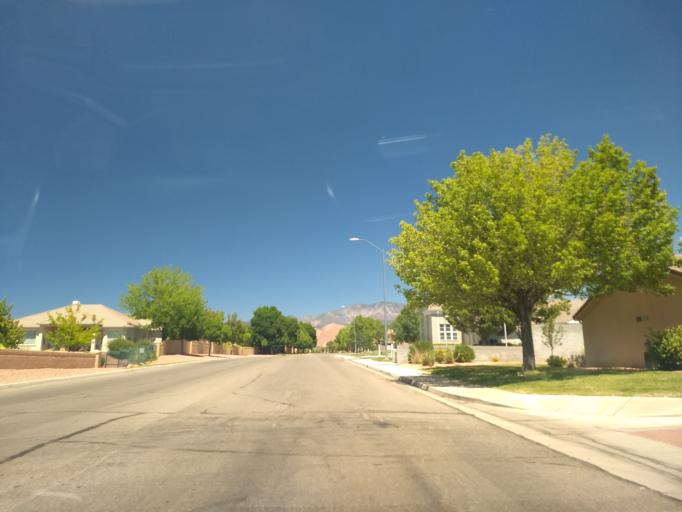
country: US
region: Utah
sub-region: Washington County
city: Washington
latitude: 37.1419
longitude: -113.5237
